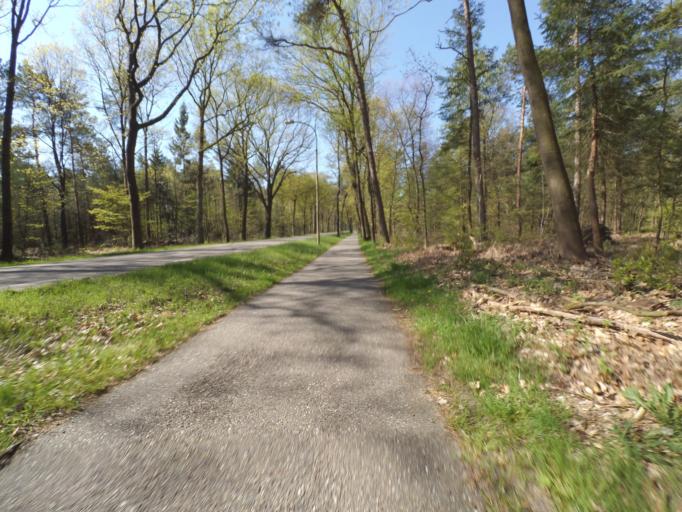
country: NL
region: Gelderland
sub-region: Gemeente Apeldoorn
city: Beekbergen
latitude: 52.1764
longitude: 5.9175
